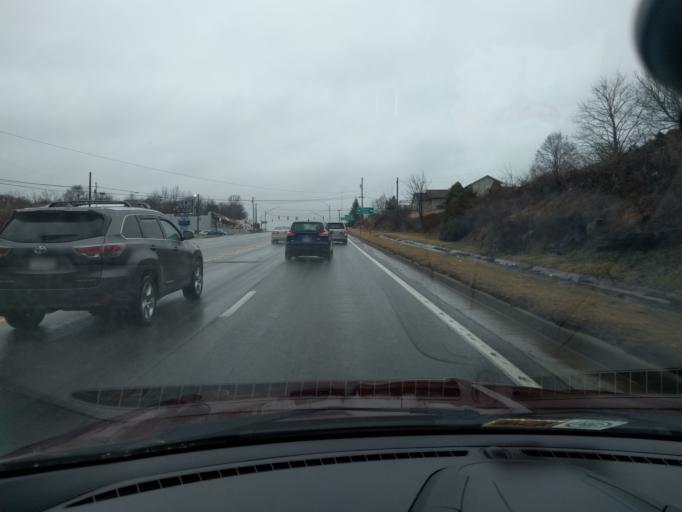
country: US
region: West Virginia
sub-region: Raleigh County
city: Beckley
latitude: 37.7919
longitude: -81.1841
